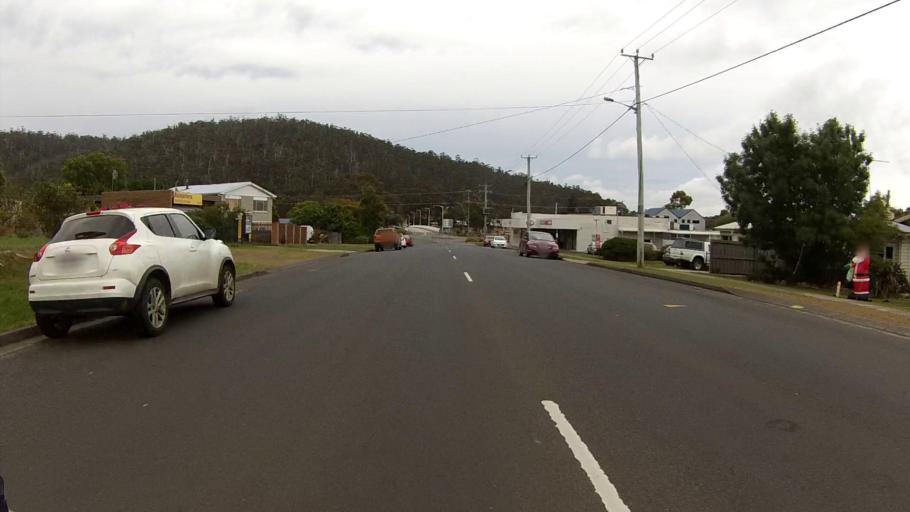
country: AU
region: Tasmania
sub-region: Sorell
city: Sorell
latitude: -42.5599
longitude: 147.8721
